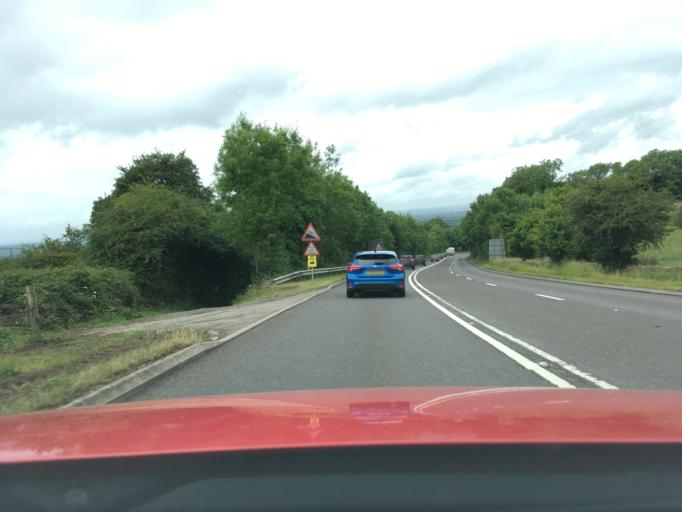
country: GB
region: England
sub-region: Worcestershire
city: Broadway
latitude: 52.0317
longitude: -1.8393
